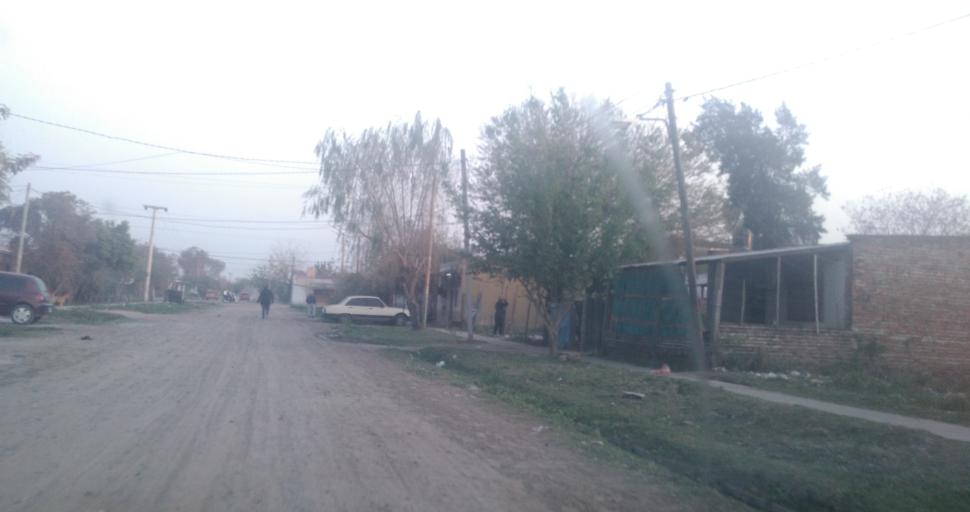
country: AR
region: Chaco
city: Resistencia
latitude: -27.4725
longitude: -59.0089
